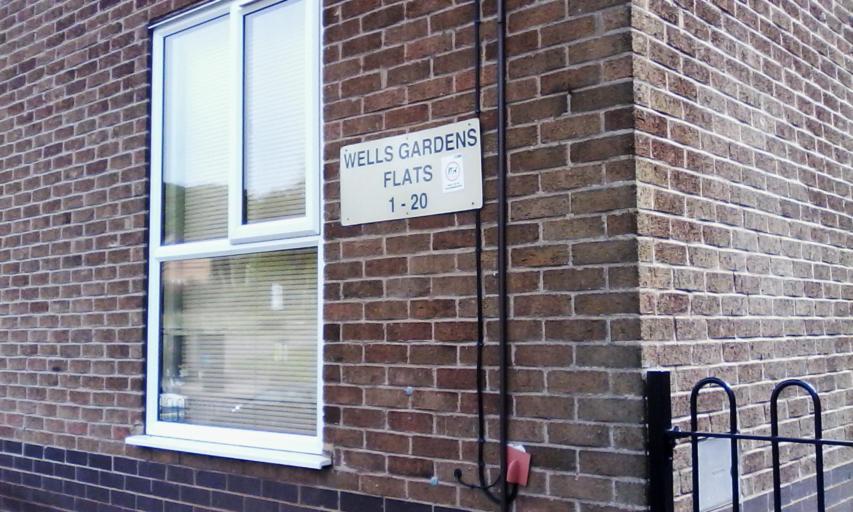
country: GB
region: England
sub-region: Nottinghamshire
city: Arnold
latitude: 52.9705
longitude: -1.1237
